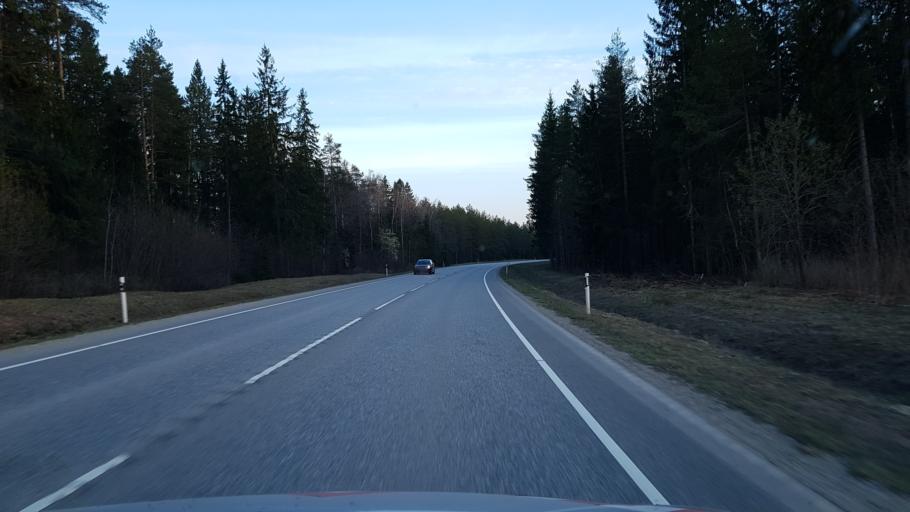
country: EE
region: Laeaene-Virumaa
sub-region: Someru vald
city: Someru
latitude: 59.3401
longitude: 26.4119
